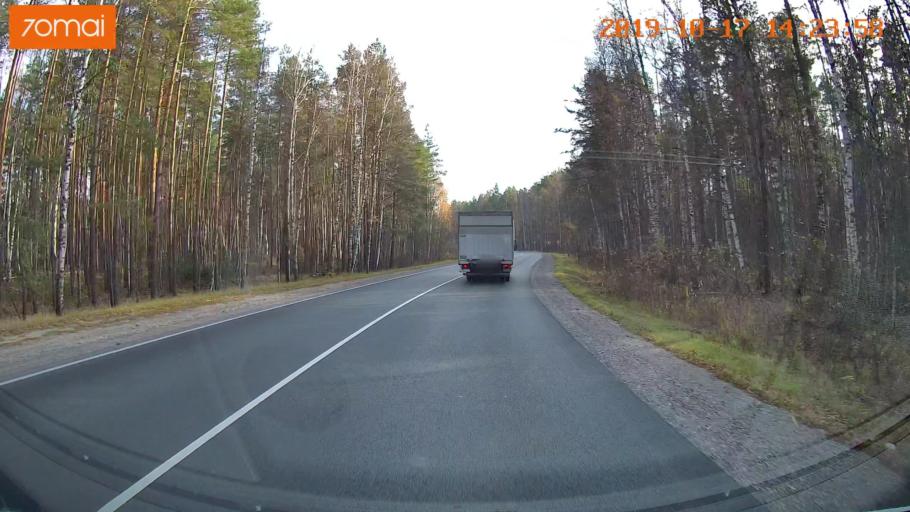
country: RU
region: Moskovskaya
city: Radovitskiy
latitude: 55.0134
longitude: 39.9639
